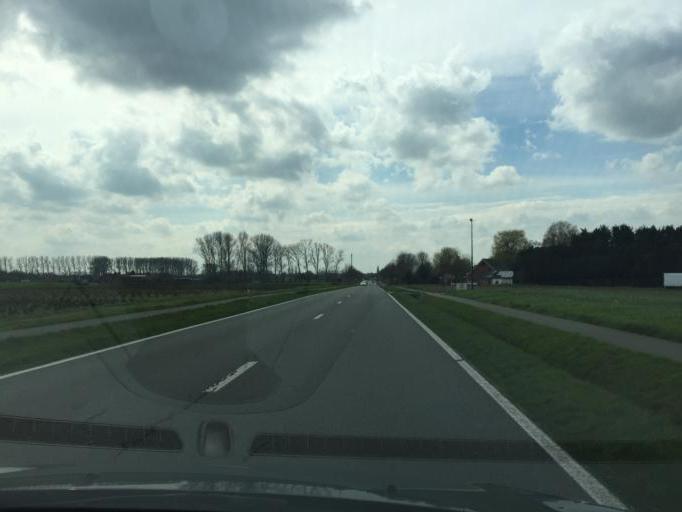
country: BE
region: Flanders
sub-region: Provincie West-Vlaanderen
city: Ruiselede
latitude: 51.0578
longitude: 3.4212
